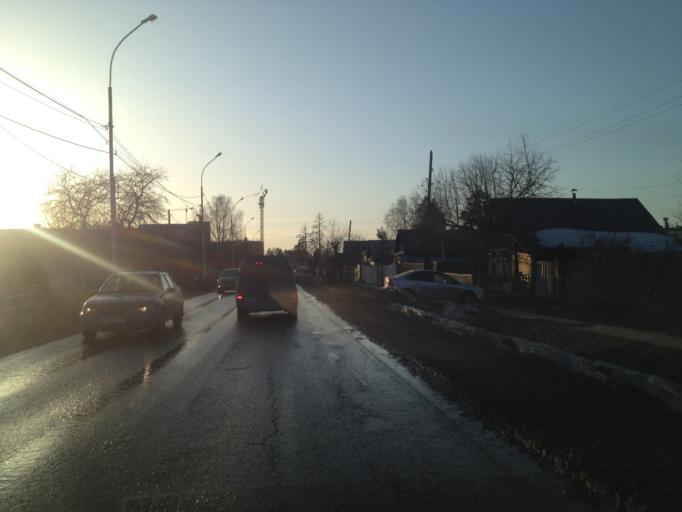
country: RU
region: Sverdlovsk
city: Sovkhoznyy
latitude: 56.7643
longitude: 60.5604
